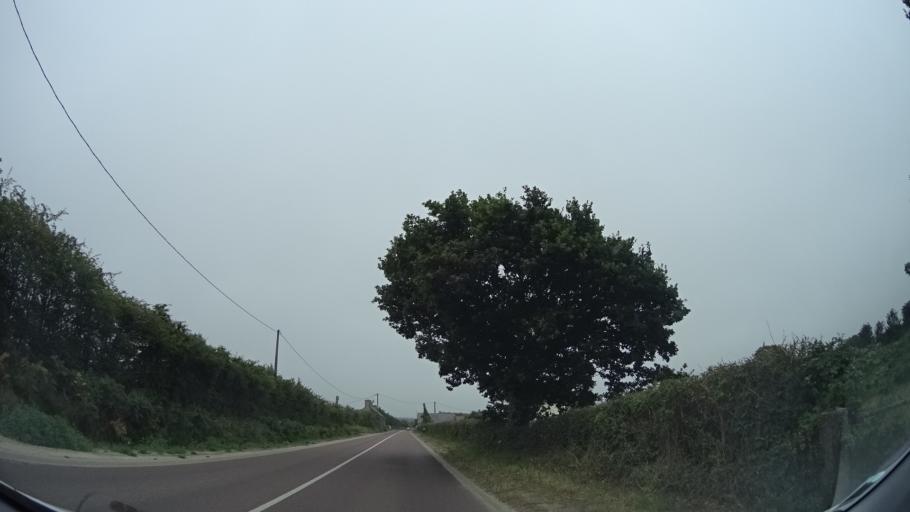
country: FR
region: Lower Normandy
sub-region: Departement de la Manche
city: Flamanville
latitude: 49.5373
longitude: -1.8330
